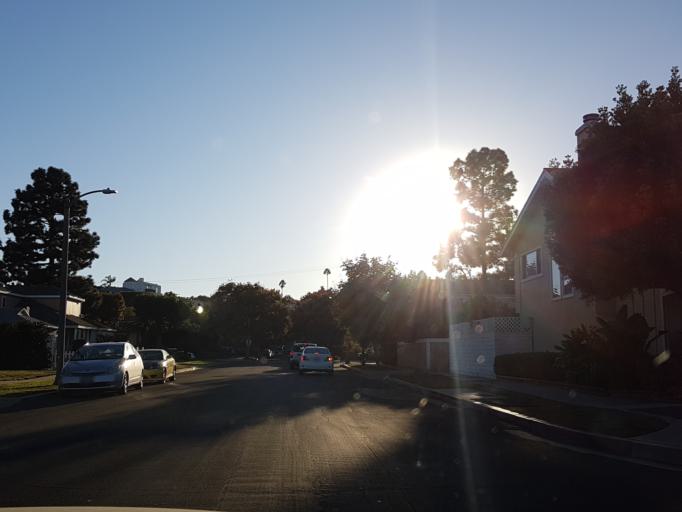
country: US
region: California
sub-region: Los Angeles County
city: Westwood, Los Angeles
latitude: 34.0201
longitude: -118.4388
